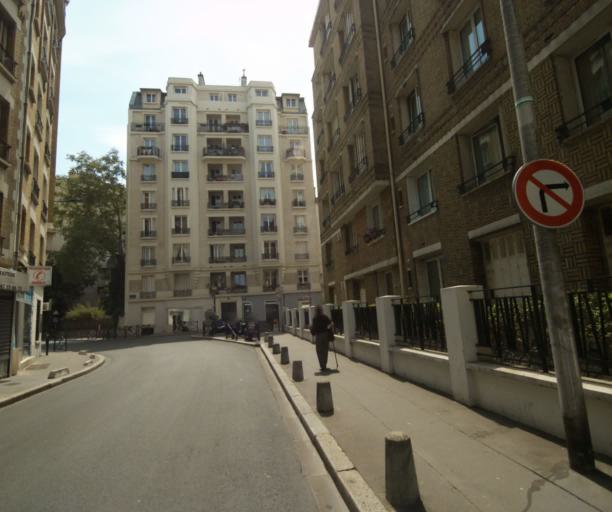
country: FR
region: Ile-de-France
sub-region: Departement des Hauts-de-Seine
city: Bois-Colombes
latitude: 48.9105
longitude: 2.2721
